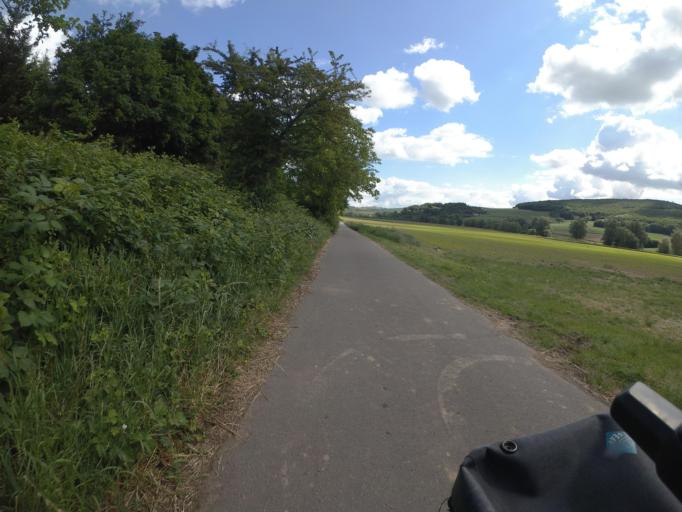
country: DE
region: Rheinland-Pfalz
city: Raumbach
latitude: 49.7245
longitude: 7.6649
